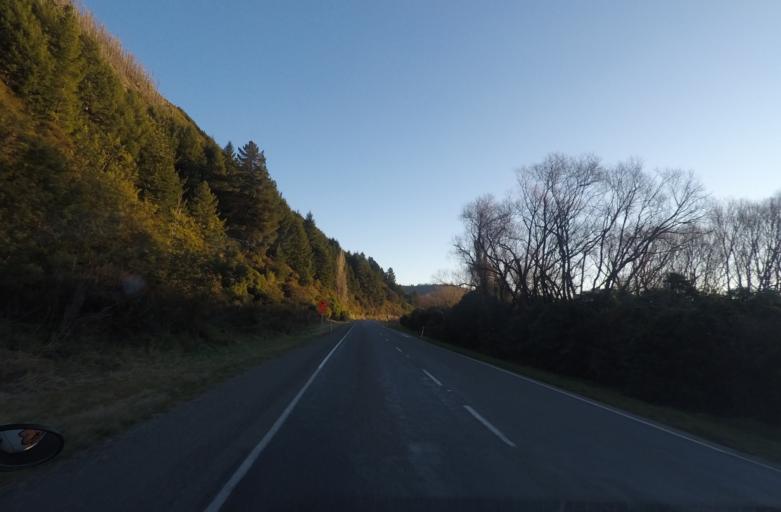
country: NZ
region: Marlborough
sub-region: Marlborough District
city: Picton
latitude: -41.2862
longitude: 173.6890
